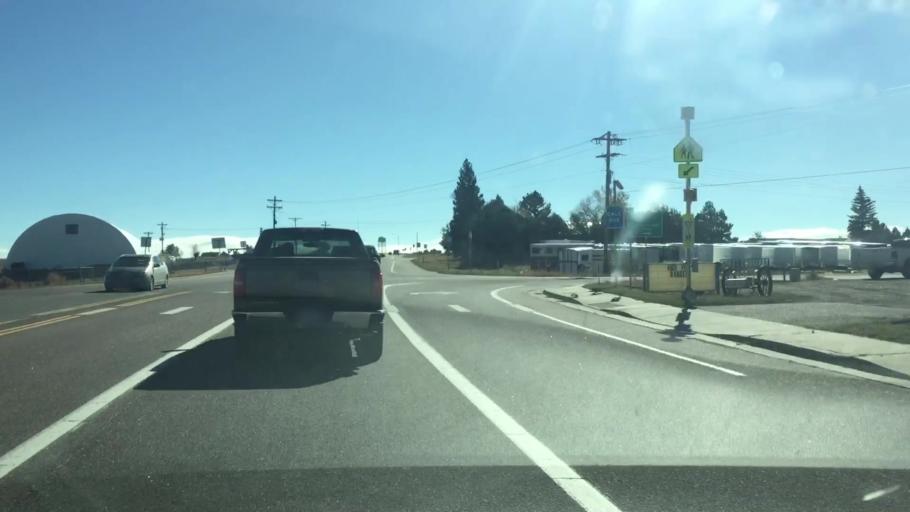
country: US
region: Colorado
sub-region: Elbert County
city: Kiowa
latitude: 39.3465
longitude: -104.4601
